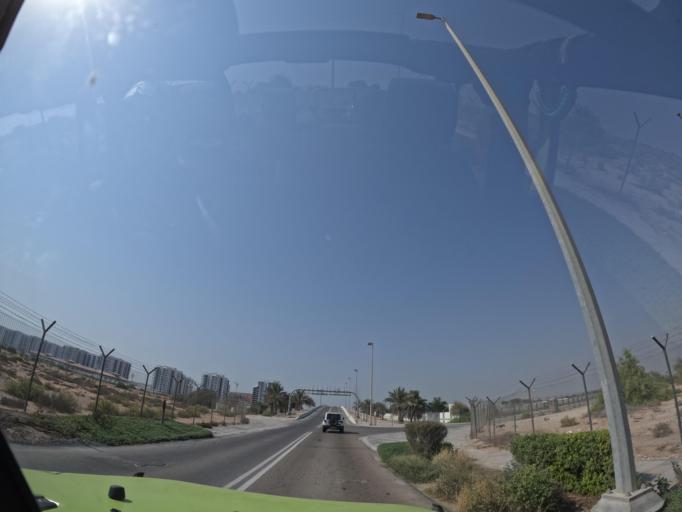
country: AE
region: Abu Dhabi
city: Abu Dhabi
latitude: 24.4792
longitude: 54.6251
